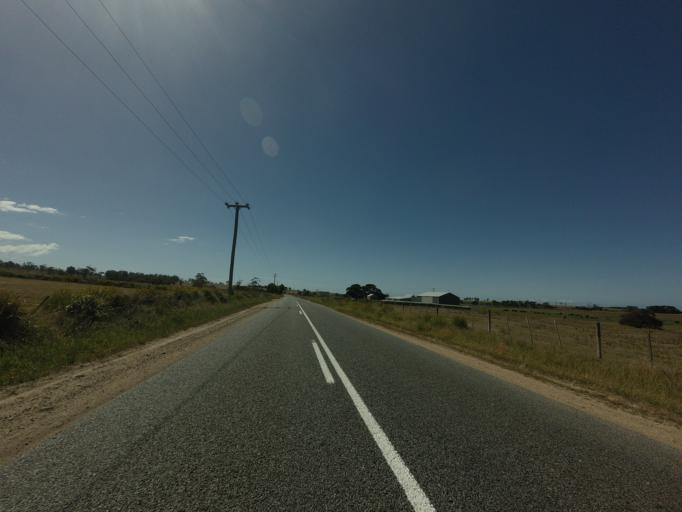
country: AU
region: Tasmania
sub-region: Break O'Day
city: St Helens
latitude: -41.7771
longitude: 148.2595
